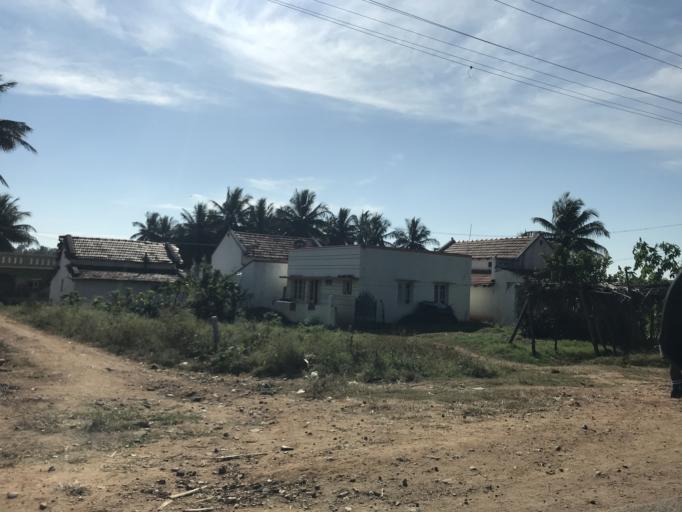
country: IN
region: Karnataka
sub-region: Mysore
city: Mysore
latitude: 12.2114
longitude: 76.5611
